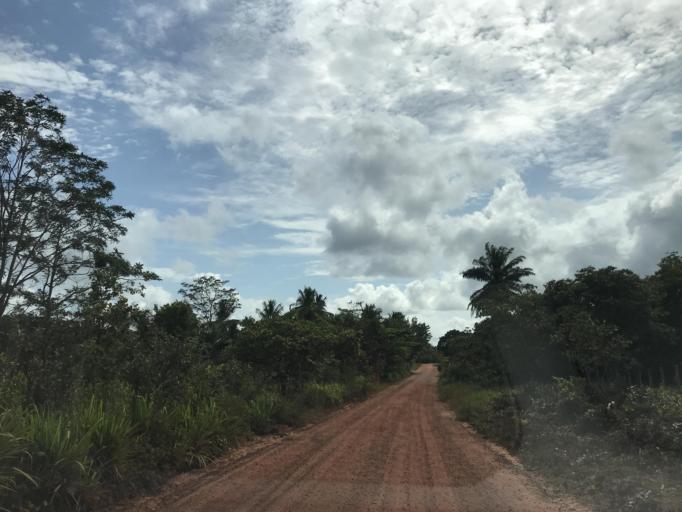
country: BR
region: Bahia
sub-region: Entre Rios
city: Entre Rios
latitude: -12.1712
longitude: -38.1483
